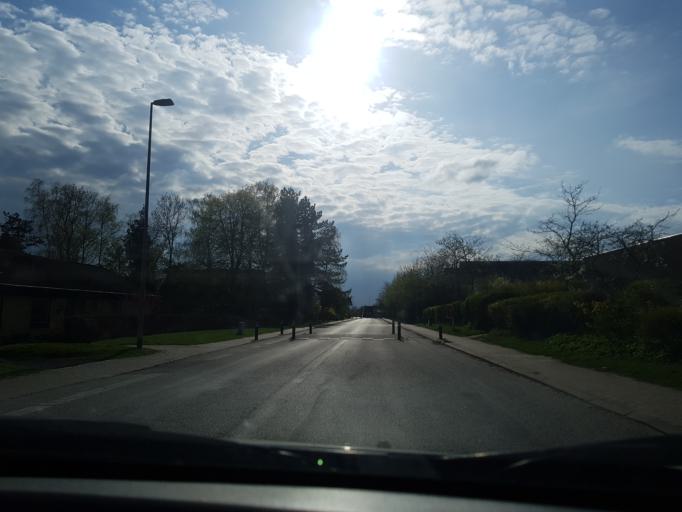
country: DK
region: Capital Region
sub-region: Allerod Kommune
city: Lillerod
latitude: 55.8595
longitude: 12.3382
